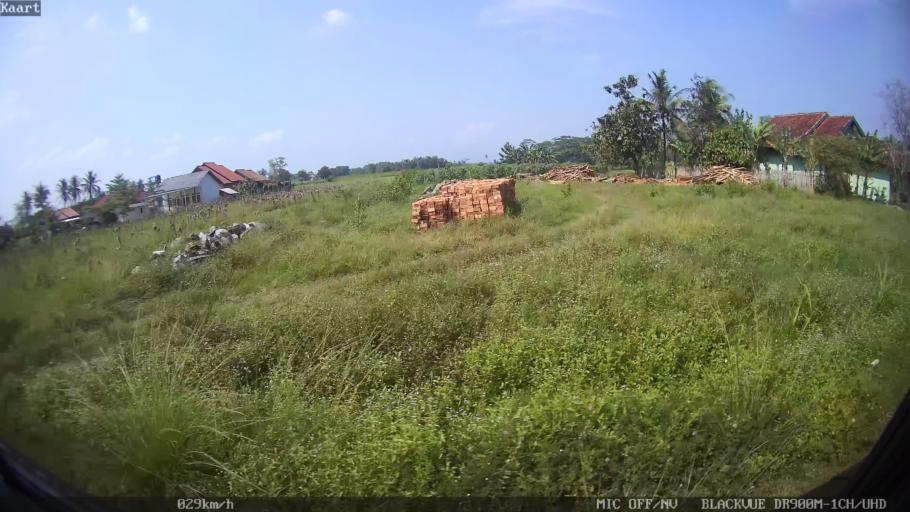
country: ID
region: Lampung
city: Natar
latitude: -5.2548
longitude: 105.2074
